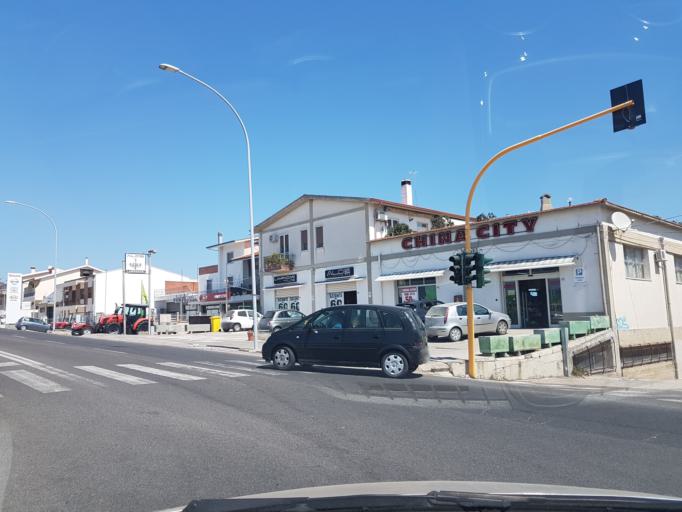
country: IT
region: Sardinia
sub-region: Provincia di Oristano
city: Santa Giusta
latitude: 39.8869
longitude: 8.6026
